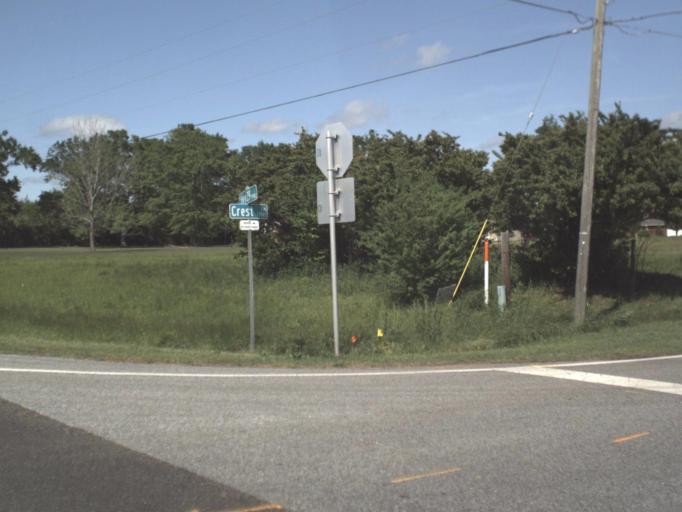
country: US
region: Florida
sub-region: Escambia County
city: Molino
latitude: 30.7081
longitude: -87.3500
